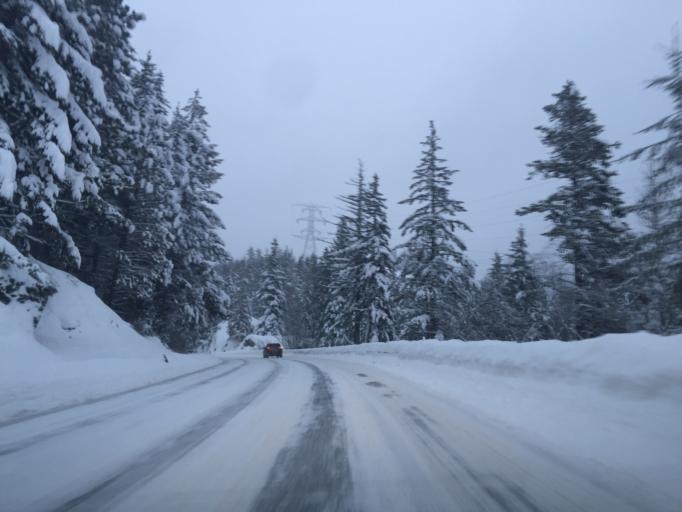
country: US
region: Washington
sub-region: Chelan County
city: Leavenworth
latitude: 47.7815
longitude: -120.9360
